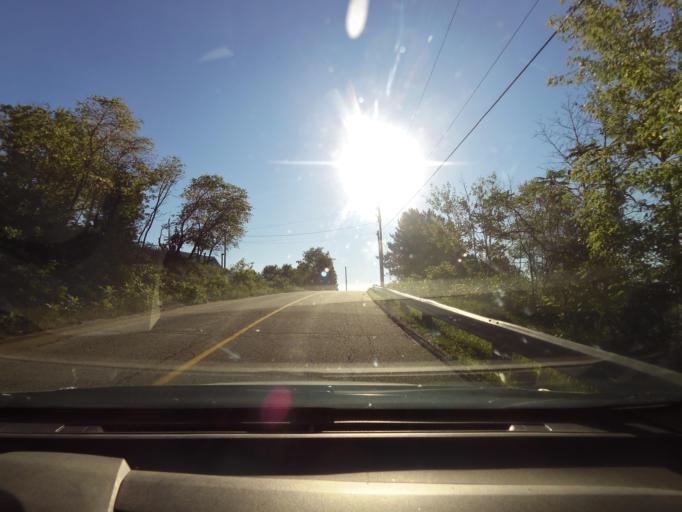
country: CA
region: Quebec
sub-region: Mauricie
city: Becancour
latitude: 46.5547
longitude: -72.3665
